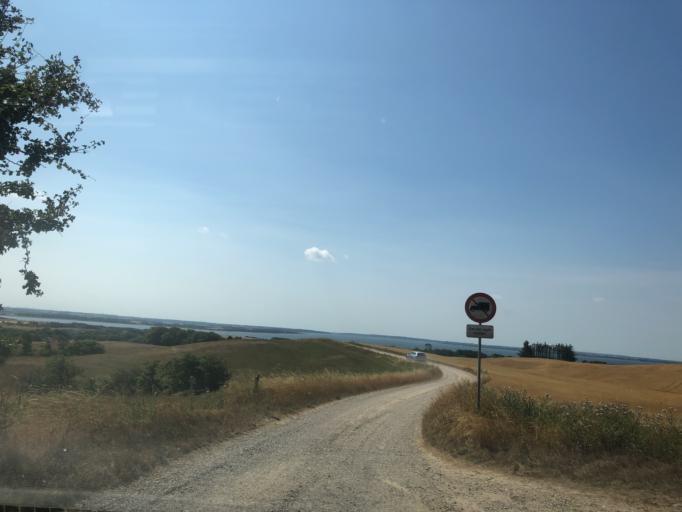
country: DK
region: North Denmark
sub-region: Morso Kommune
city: Nykobing Mors
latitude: 56.8315
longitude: 9.0003
